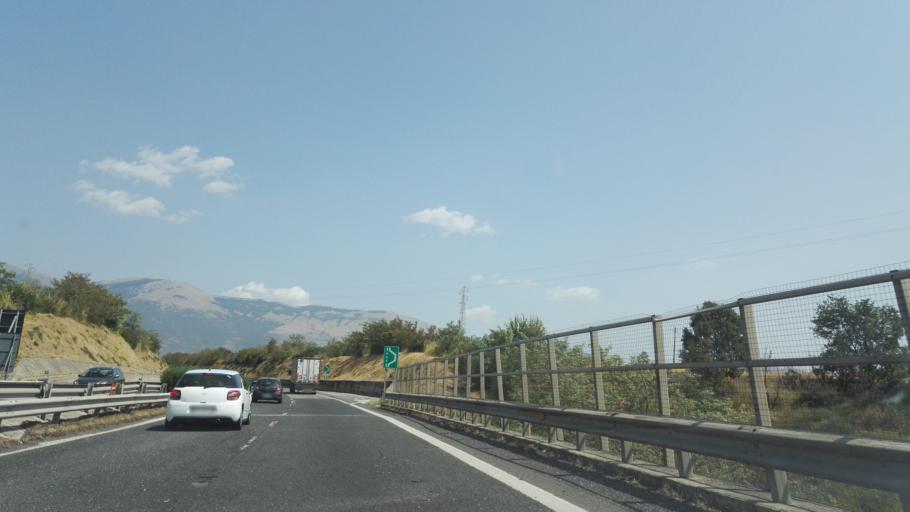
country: IT
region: Calabria
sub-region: Provincia di Cosenza
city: Castrovillari
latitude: 39.7677
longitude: 16.2235
